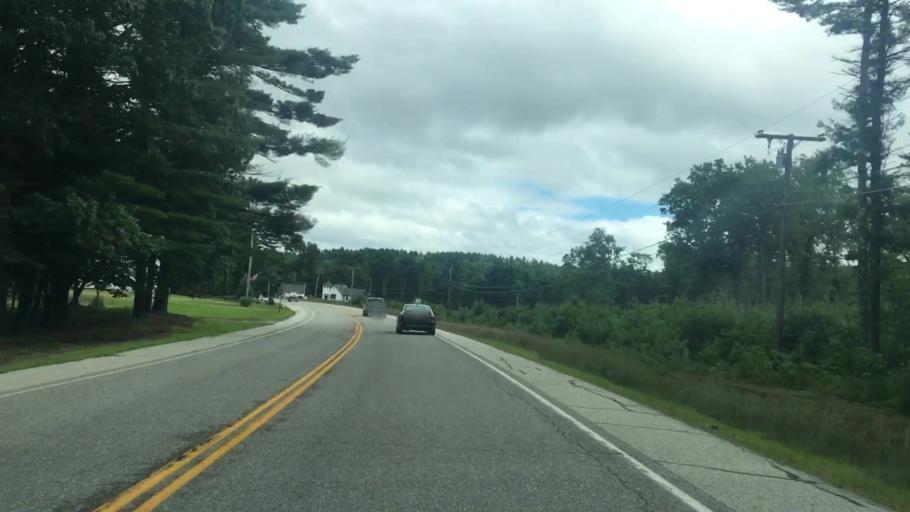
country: US
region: Maine
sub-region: York County
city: Lake Arrowhead
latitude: 43.6227
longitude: -70.7383
